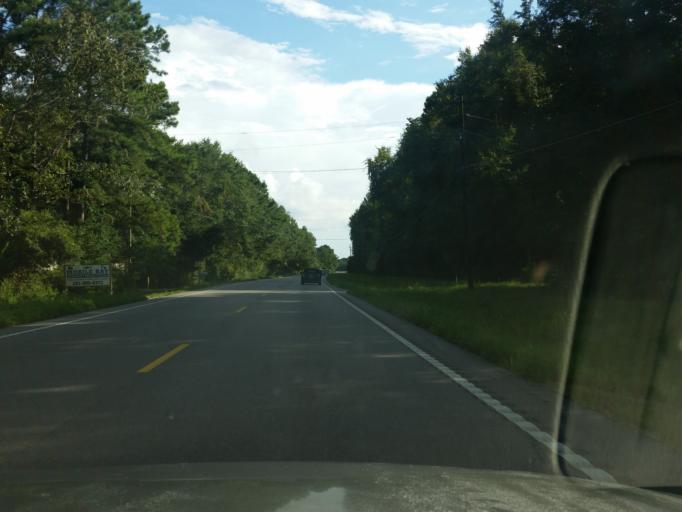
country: US
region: Alabama
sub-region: Mobile County
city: Bayou La Batre
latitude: 30.4030
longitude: -88.1080
